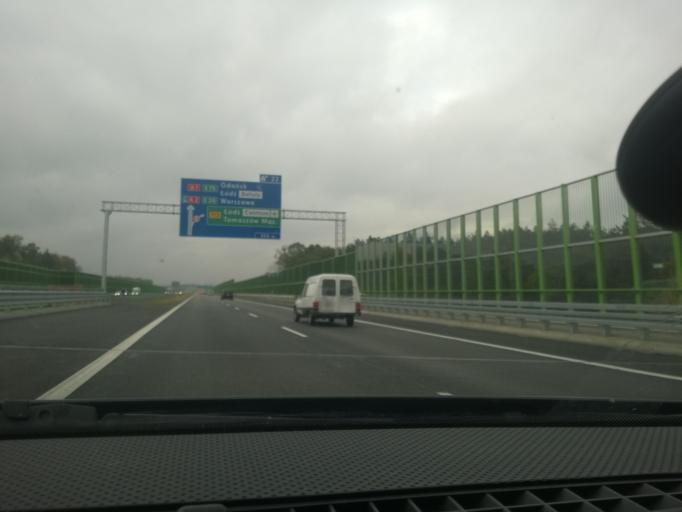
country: PL
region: Lodz Voivodeship
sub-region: Powiat lodzki wschodni
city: Andrespol
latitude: 51.7378
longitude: 19.6014
